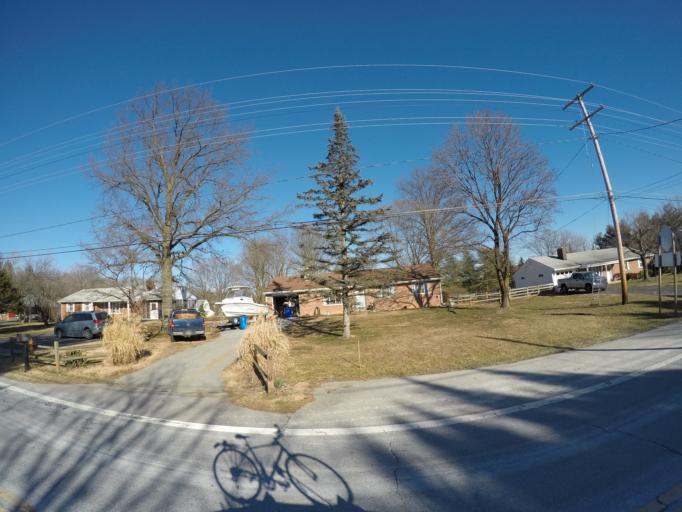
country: US
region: Maryland
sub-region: Howard County
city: Ilchester
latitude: 39.2186
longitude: -76.7876
